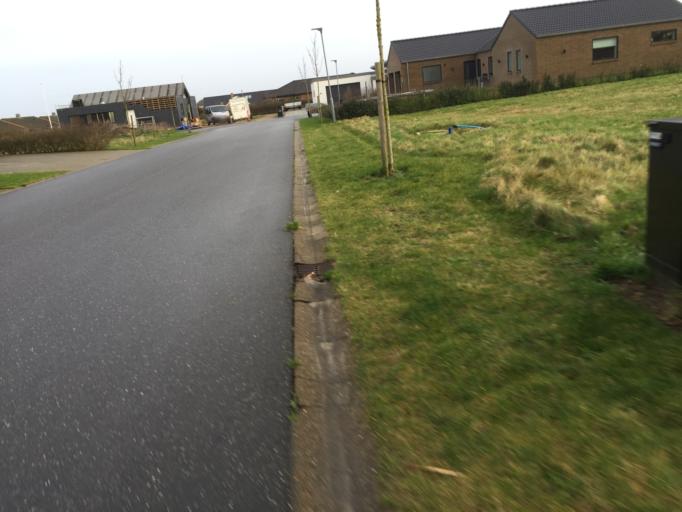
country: DK
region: Central Jutland
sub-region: Ringkobing-Skjern Kommune
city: Ringkobing
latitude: 56.1002
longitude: 8.2623
